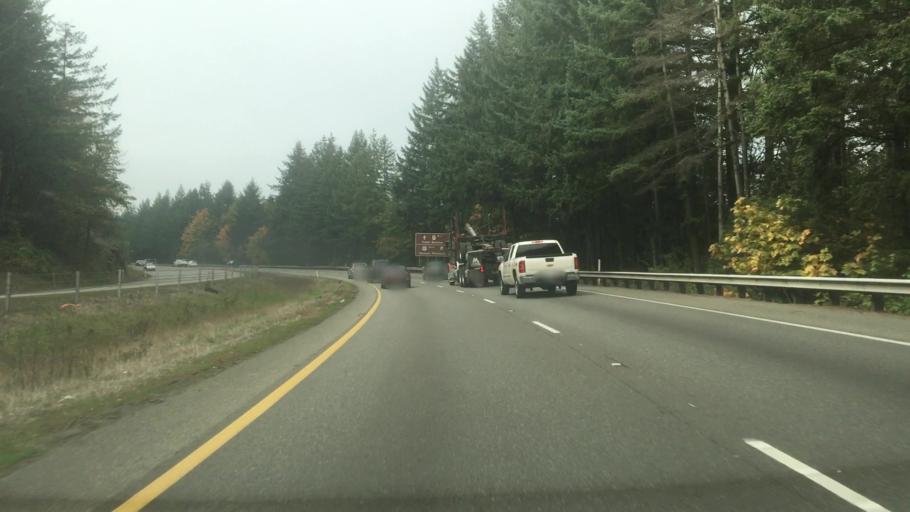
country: US
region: Washington
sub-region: Thurston County
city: Olympia
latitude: 47.0547
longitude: -123.0052
